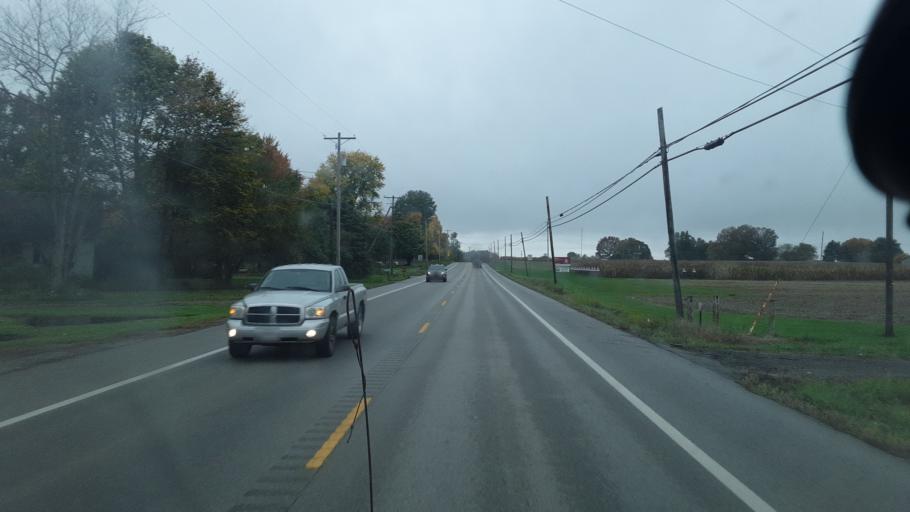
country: US
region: Ohio
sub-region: Wayne County
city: Wooster
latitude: 40.7646
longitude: -81.8996
